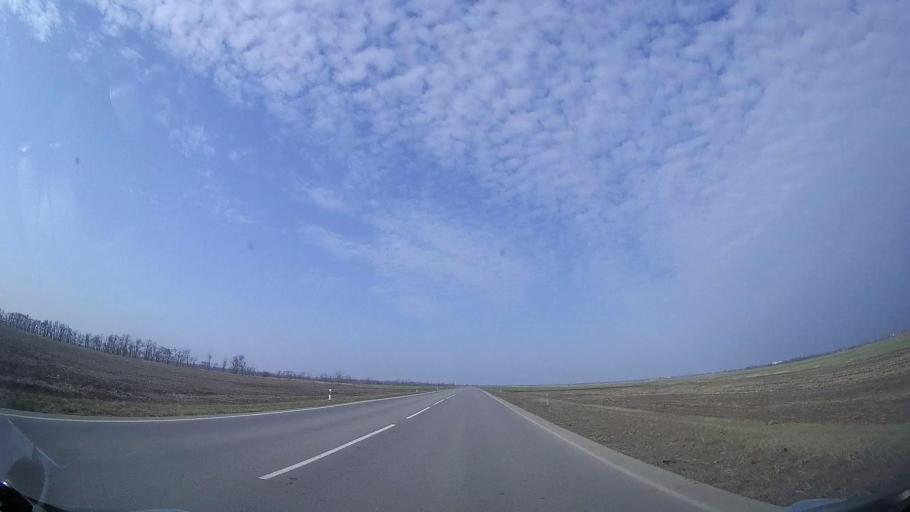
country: RU
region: Rostov
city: Tselina
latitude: 46.5126
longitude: 41.0611
